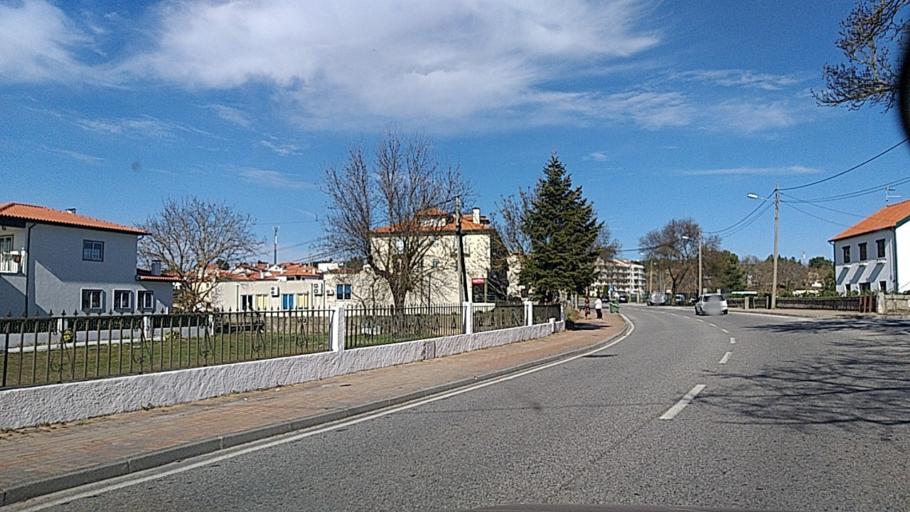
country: PT
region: Guarda
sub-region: Guarda
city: Sequeira
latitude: 40.5575
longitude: -7.2363
